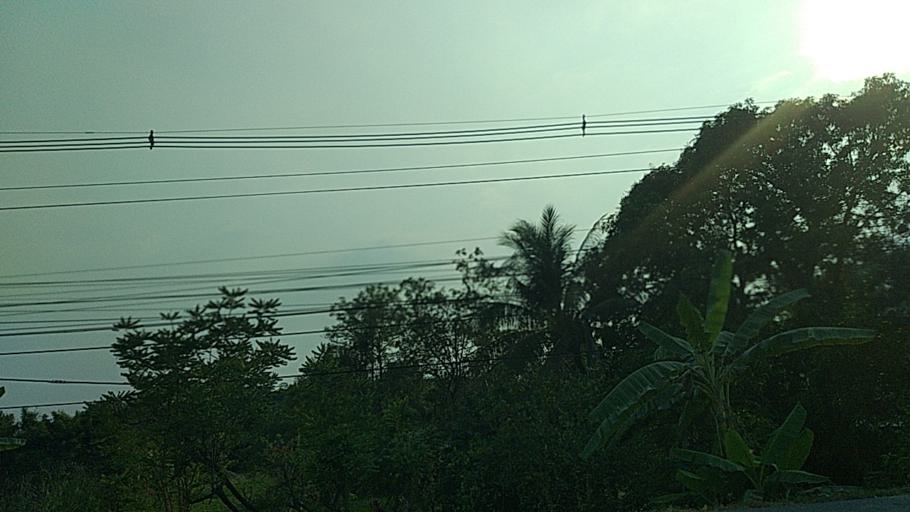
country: TH
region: Nakhon Nayok
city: Nakhon Nayok
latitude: 14.2077
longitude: 101.1834
